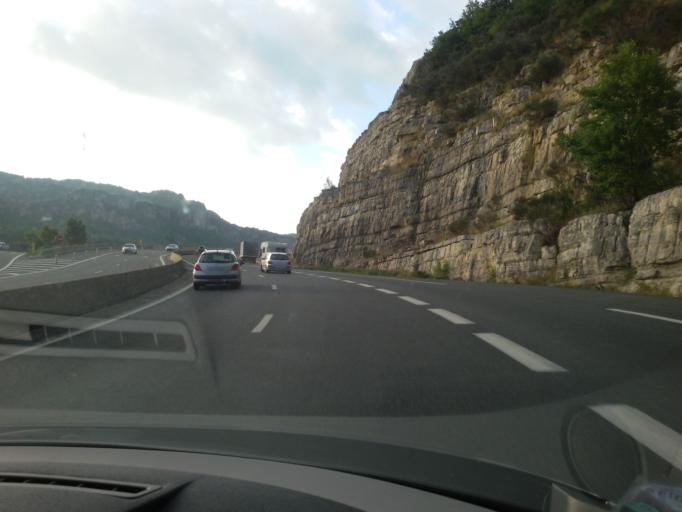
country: FR
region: Languedoc-Roussillon
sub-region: Departement de l'Herault
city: Lodeve
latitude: 43.8147
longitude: 3.3200
